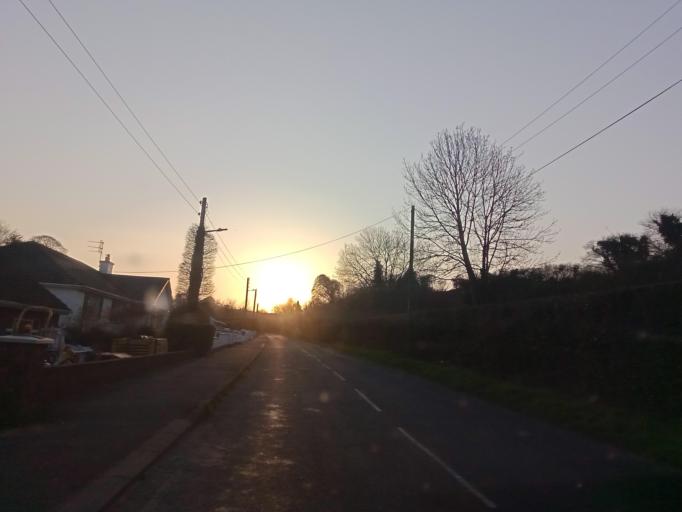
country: IE
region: Leinster
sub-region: Kilkenny
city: Castlecomer
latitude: 52.8081
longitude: -7.2149
